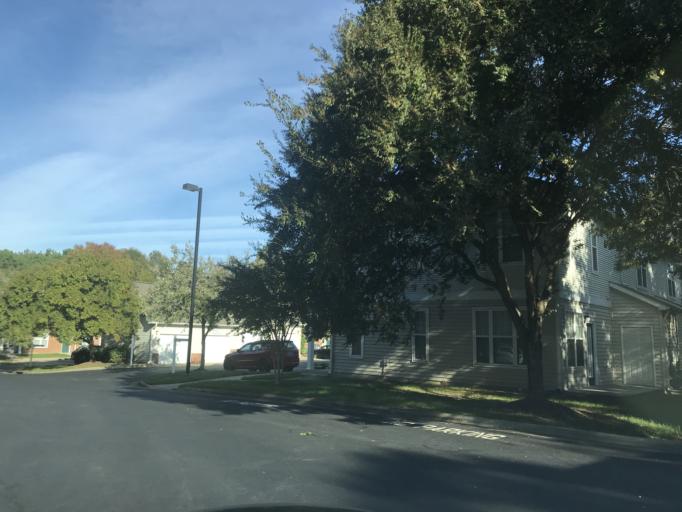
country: US
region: North Carolina
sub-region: Wake County
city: Wake Forest
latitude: 35.8991
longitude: -78.5529
